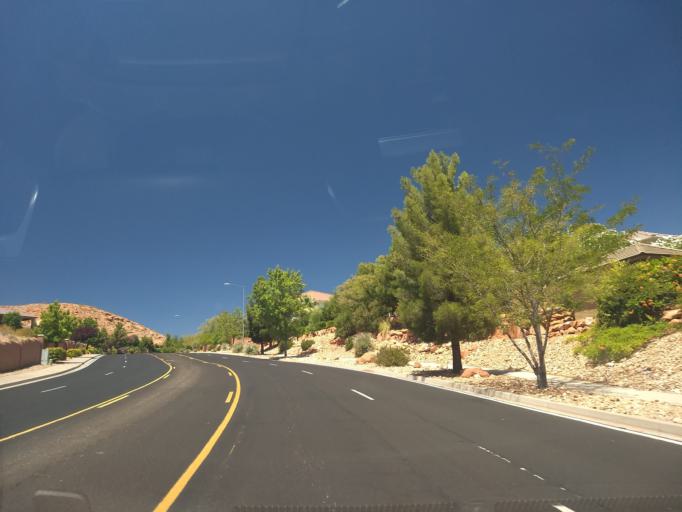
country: US
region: Utah
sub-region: Washington County
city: Washington
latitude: 37.1437
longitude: -113.5289
